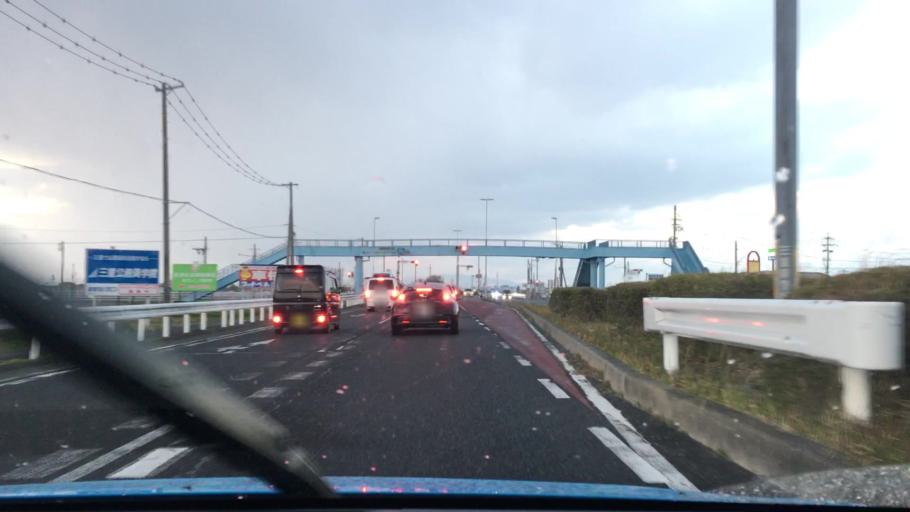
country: JP
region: Mie
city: Ise
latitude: 34.5682
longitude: 136.6342
